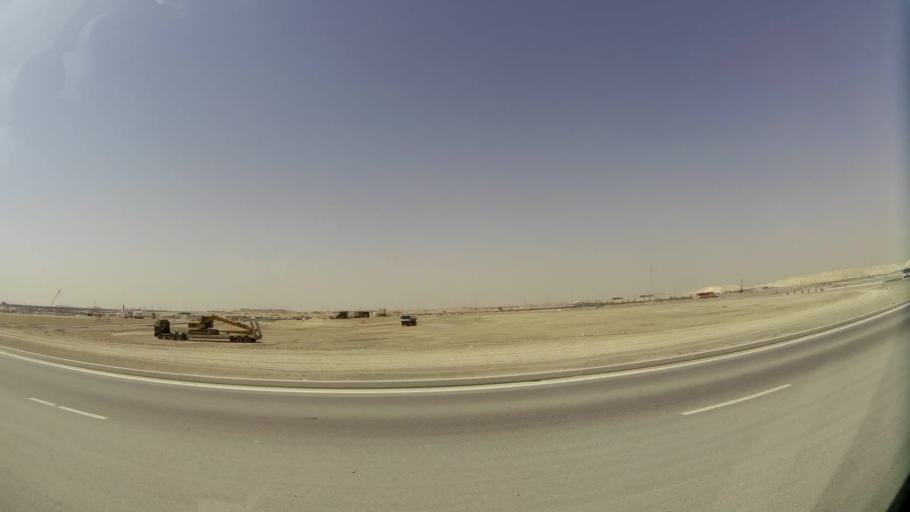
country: QA
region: Baladiyat Umm Salal
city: Umm Salal Muhammad
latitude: 25.4055
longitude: 51.4961
